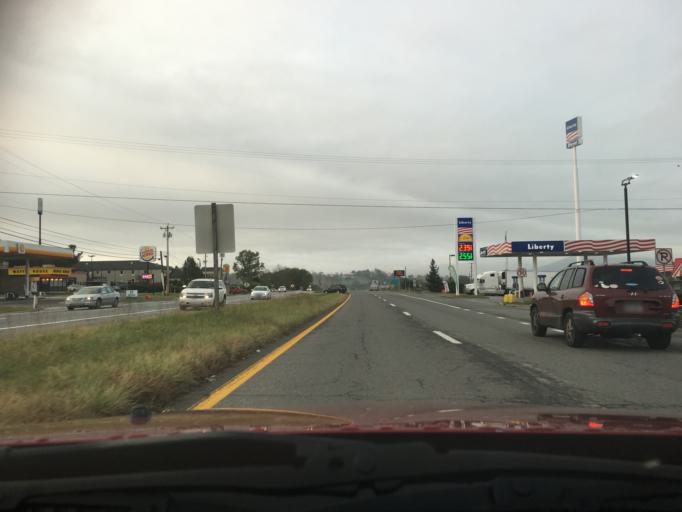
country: US
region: Virginia
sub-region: Pulaski County
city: Dublin
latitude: 37.0834
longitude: -80.6903
